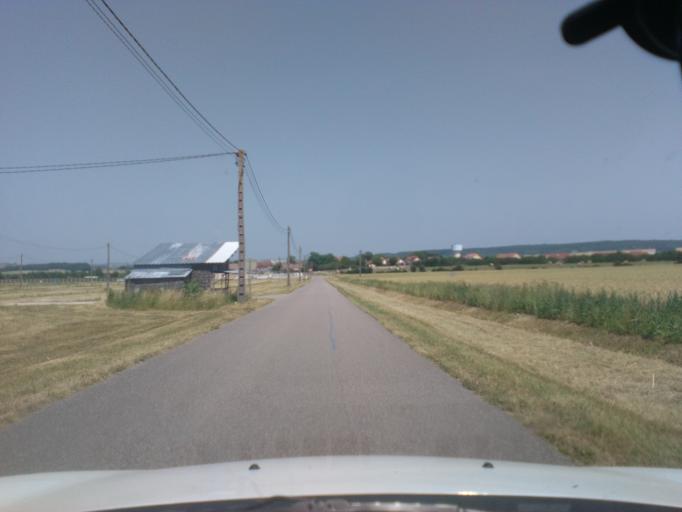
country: FR
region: Lorraine
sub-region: Departement des Vosges
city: Mirecourt
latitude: 48.3165
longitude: 6.1162
